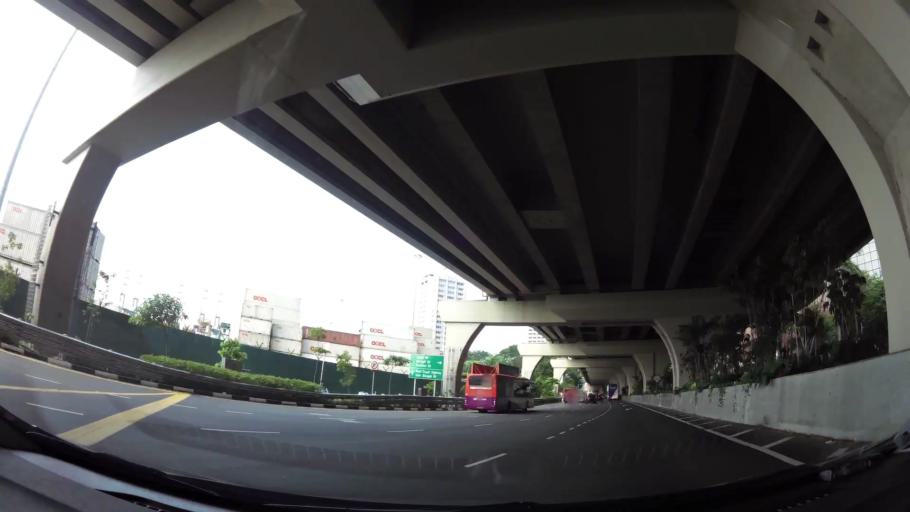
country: SG
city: Singapore
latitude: 1.2727
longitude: 103.8452
